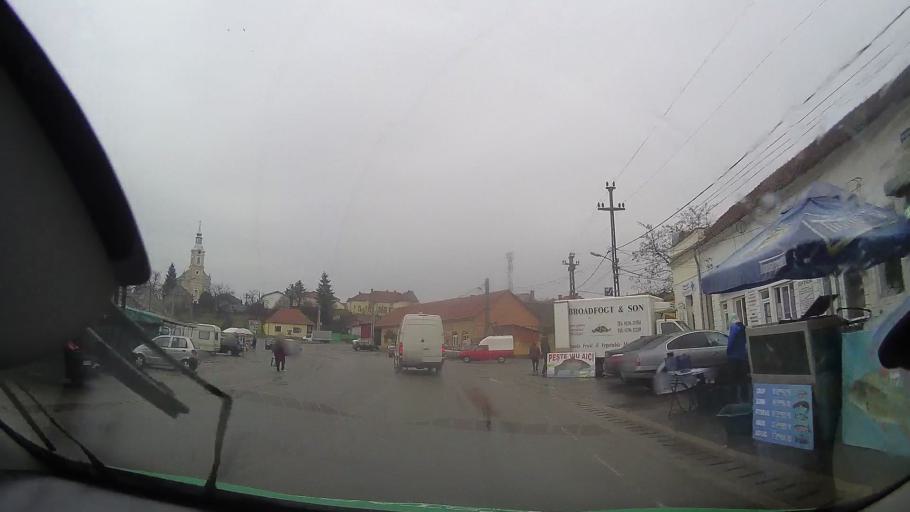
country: RO
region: Bihor
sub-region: Comuna Tinca
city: Tinca
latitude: 46.7722
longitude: 21.9303
